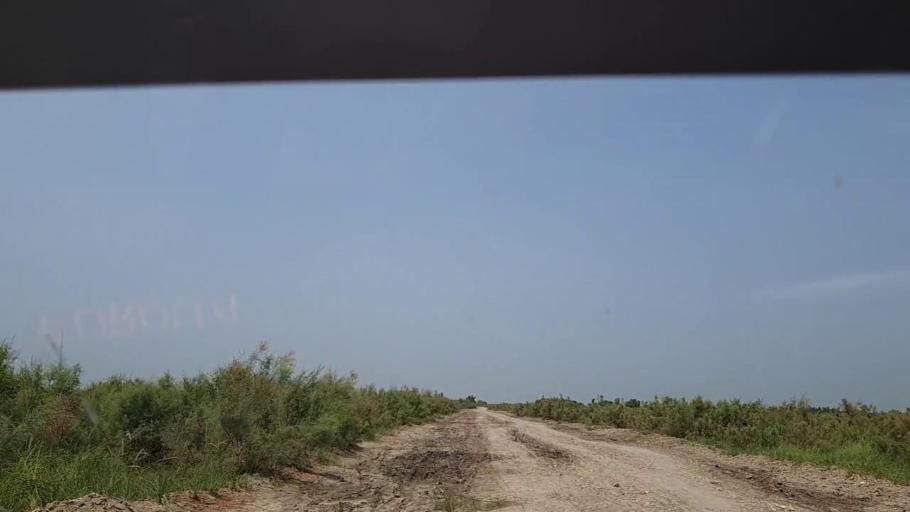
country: PK
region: Sindh
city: Adilpur
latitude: 27.8980
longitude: 69.2371
